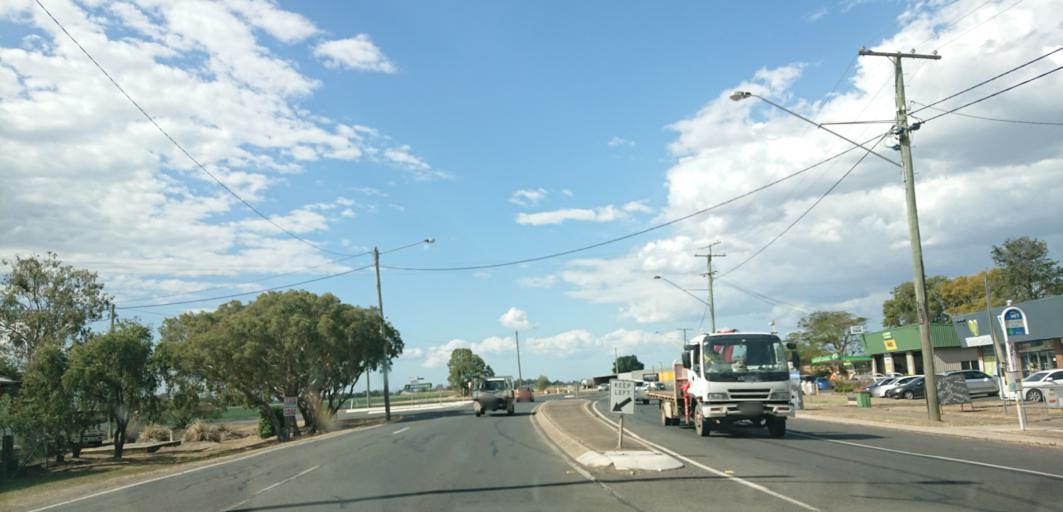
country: AU
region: Queensland
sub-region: Lockyer Valley
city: Gatton
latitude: -27.5551
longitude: 152.2887
